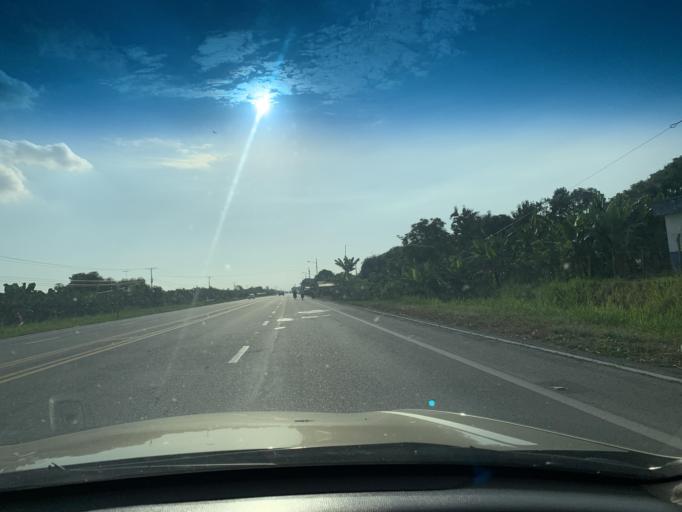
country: EC
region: Guayas
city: Naranjito
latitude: -2.2571
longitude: -79.5802
